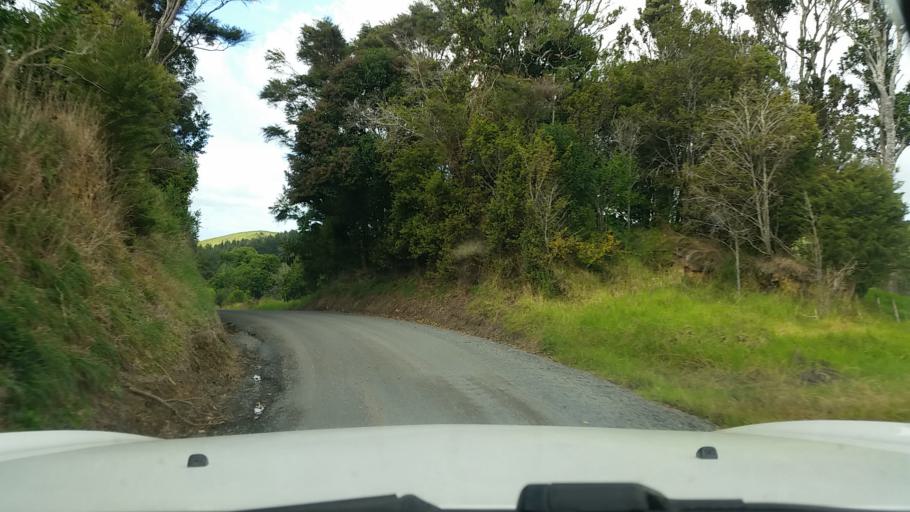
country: NZ
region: Waikato
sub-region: Hauraki District
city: Ngatea
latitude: -37.4477
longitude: 175.4788
